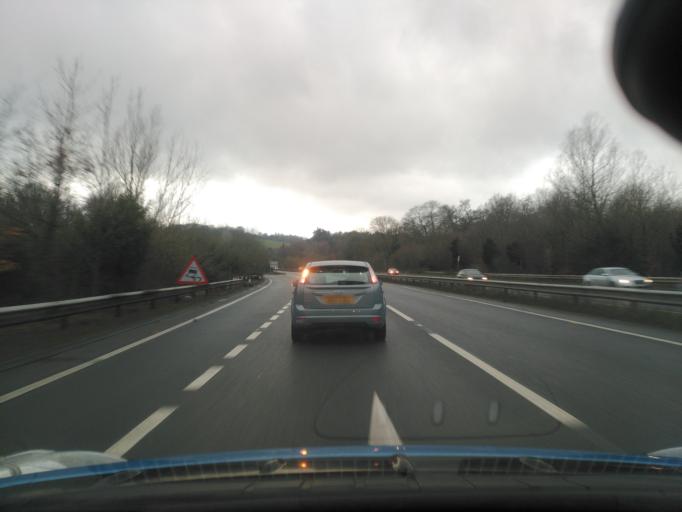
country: GB
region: England
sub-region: Surrey
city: Godalming
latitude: 51.2234
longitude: -0.6310
